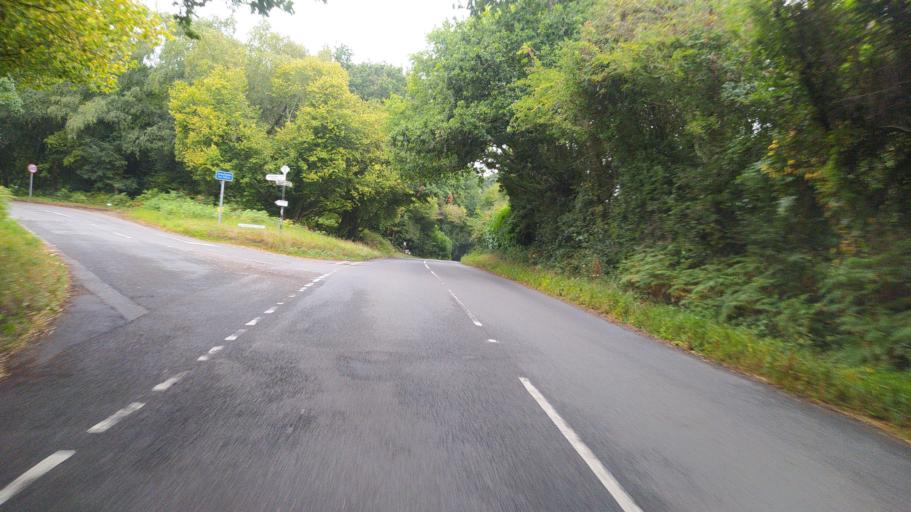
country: GB
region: England
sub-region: Dorset
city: Verwood
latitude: 50.8857
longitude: -1.9072
